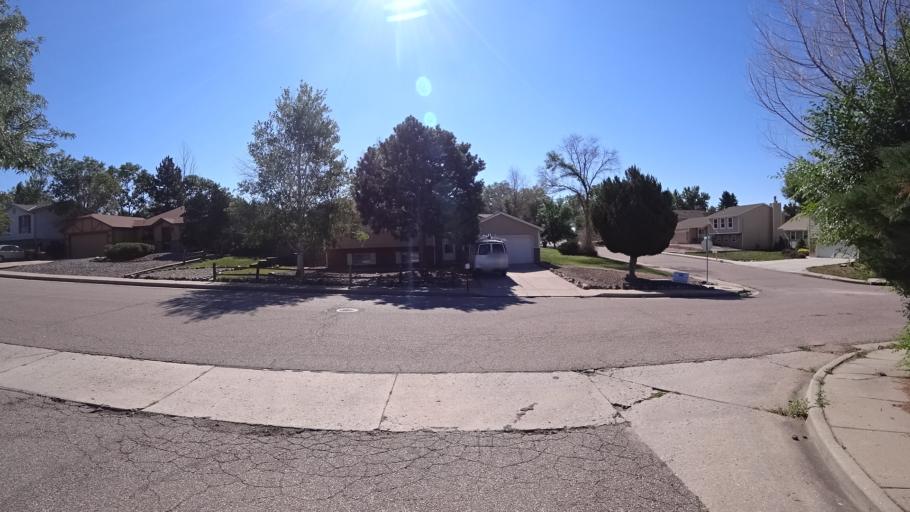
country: US
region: Colorado
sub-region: El Paso County
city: Air Force Academy
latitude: 38.9433
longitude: -104.7929
